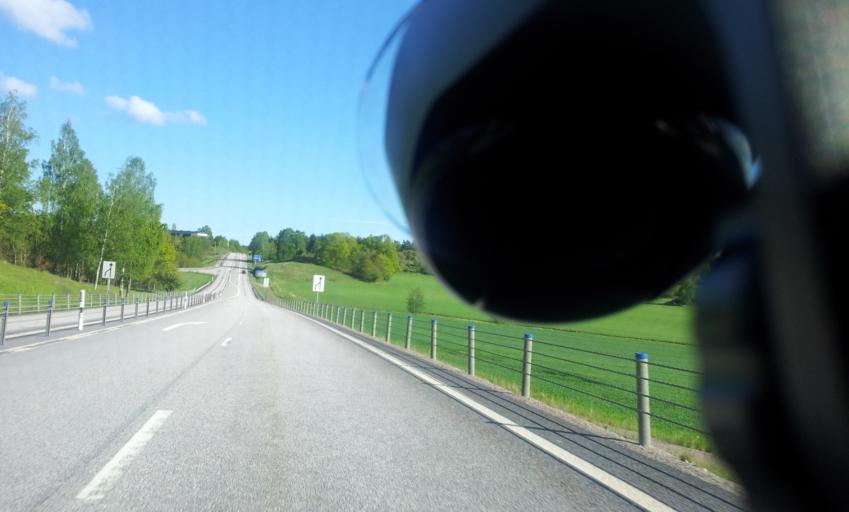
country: SE
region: Kalmar
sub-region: Vasterviks Kommun
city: Gamleby
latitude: 57.8736
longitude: 16.4053
